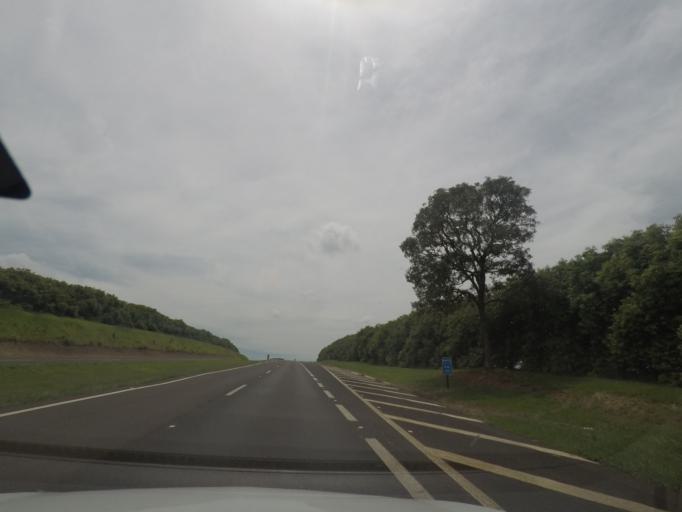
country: BR
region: Sao Paulo
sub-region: Bebedouro
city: Bebedouro
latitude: -21.0128
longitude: -48.4264
